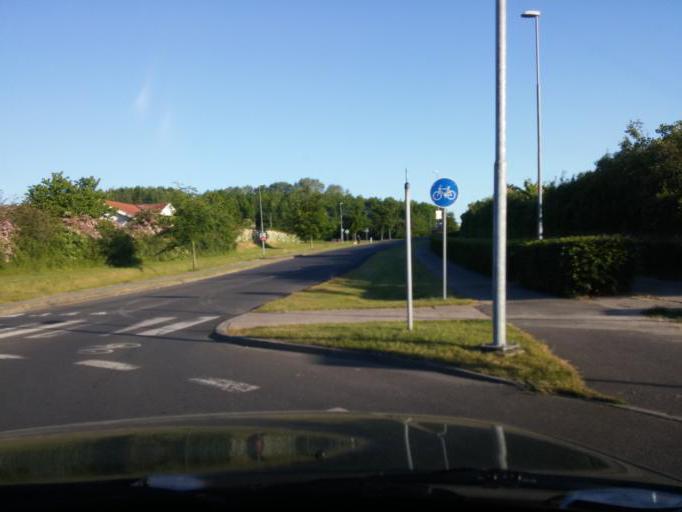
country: DK
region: South Denmark
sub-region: Kerteminde Kommune
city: Munkebo
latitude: 55.4478
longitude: 10.5445
